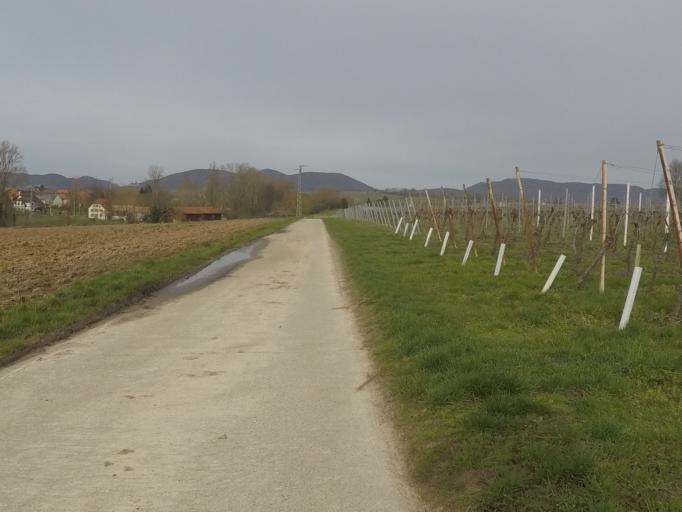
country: DE
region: Rheinland-Pfalz
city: Heuchelheim-Klingen
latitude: 49.1406
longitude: 8.0653
